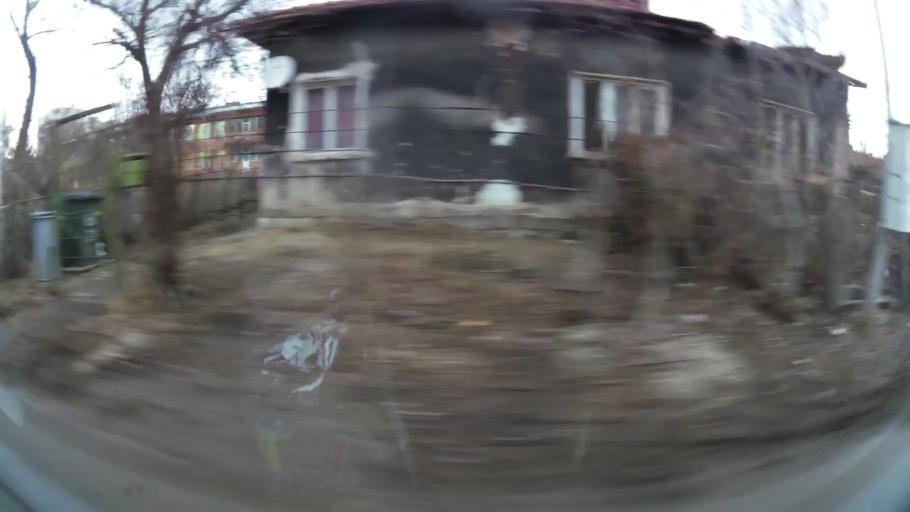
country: BG
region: Sofia-Capital
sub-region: Stolichna Obshtina
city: Sofia
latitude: 42.7358
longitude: 23.2959
